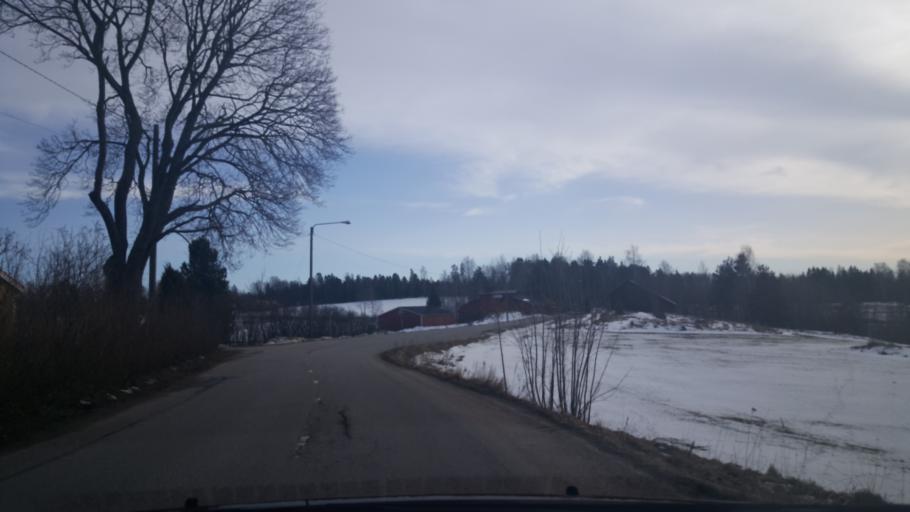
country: FI
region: Uusimaa
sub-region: Helsinki
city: Teekkarikylae
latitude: 60.2900
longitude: 24.8917
